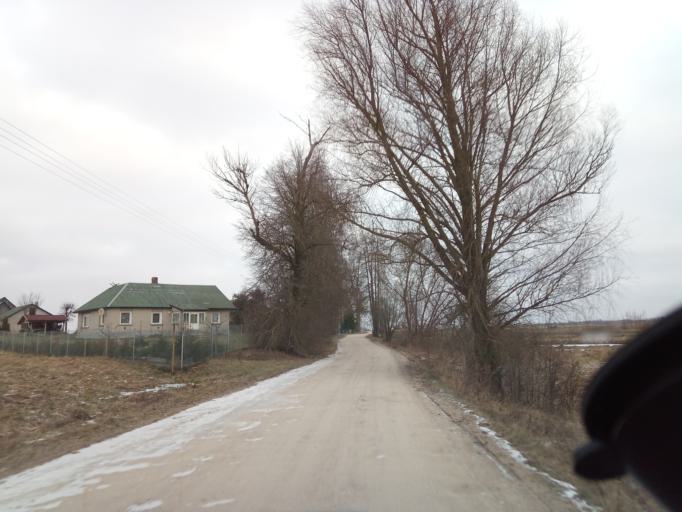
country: LT
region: Alytaus apskritis
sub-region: Alytaus rajonas
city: Daugai
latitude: 54.3674
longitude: 24.4472
